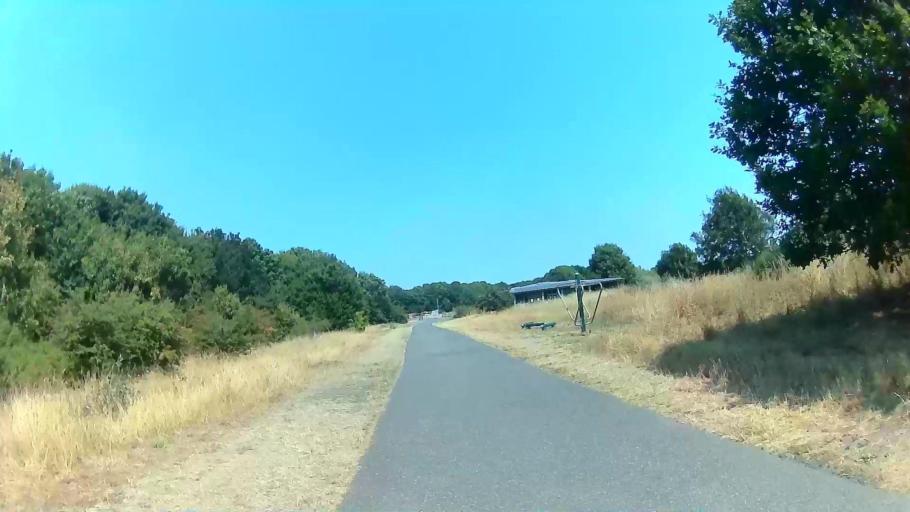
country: GB
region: England
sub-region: Greater London
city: Elm Park
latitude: 51.5402
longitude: 0.2142
